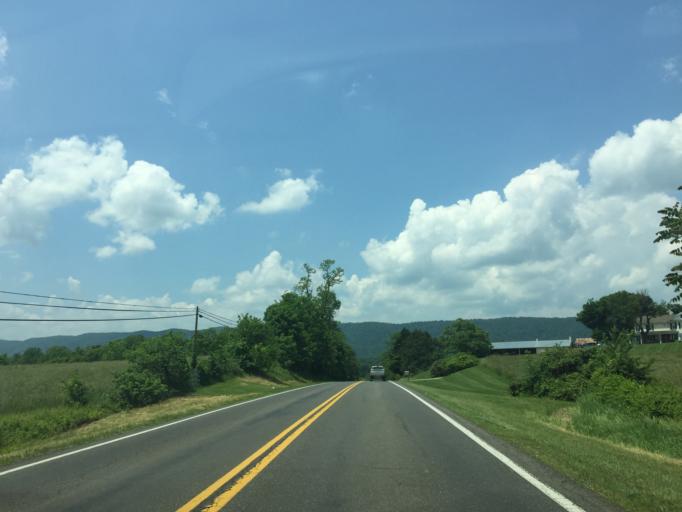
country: US
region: Virginia
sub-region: Shenandoah County
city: Strasburg
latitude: 39.0331
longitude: -78.3767
